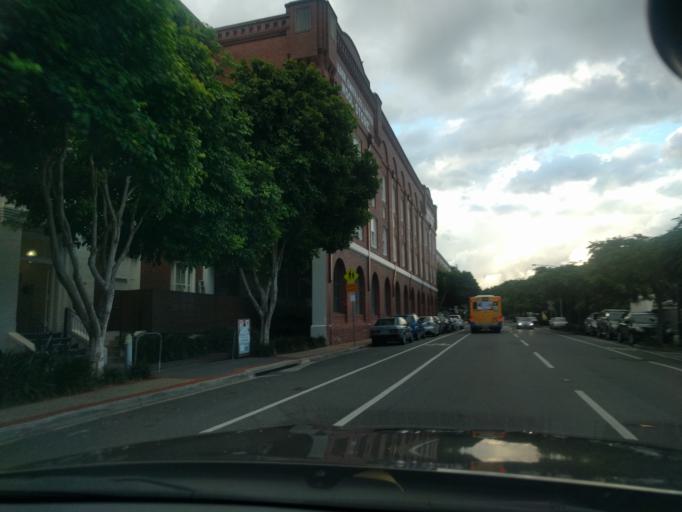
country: AU
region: Queensland
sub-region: Brisbane
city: Balmoral
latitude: -27.4599
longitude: 153.0501
